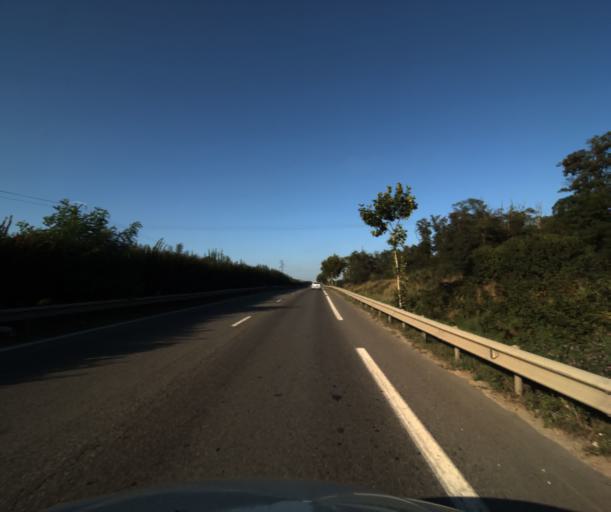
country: FR
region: Midi-Pyrenees
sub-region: Departement de la Haute-Garonne
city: Saubens
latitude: 43.4949
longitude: 1.3459
